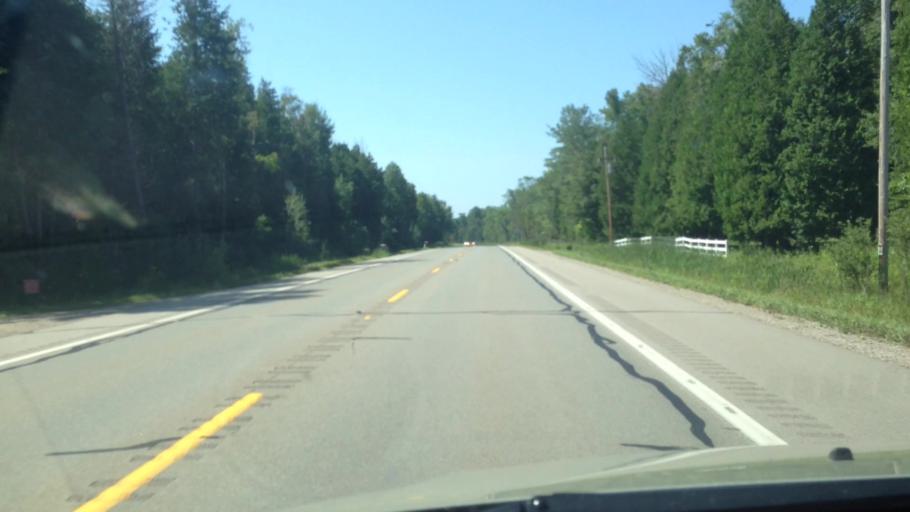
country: US
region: Michigan
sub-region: Menominee County
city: Menominee
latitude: 45.3131
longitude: -87.4357
